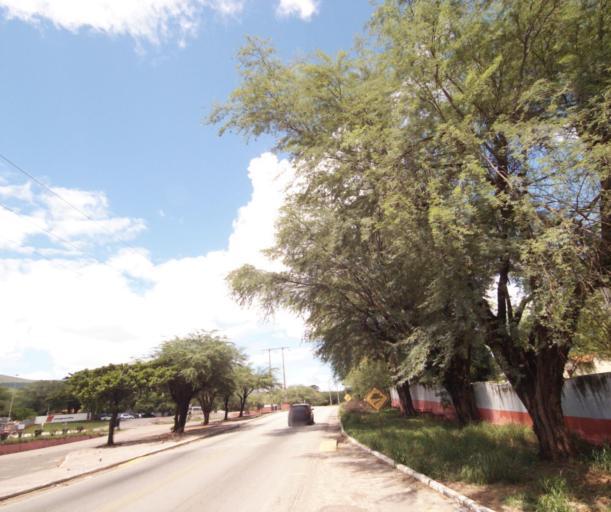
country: BR
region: Bahia
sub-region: Brumado
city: Brumado
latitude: -14.2399
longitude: -41.7233
